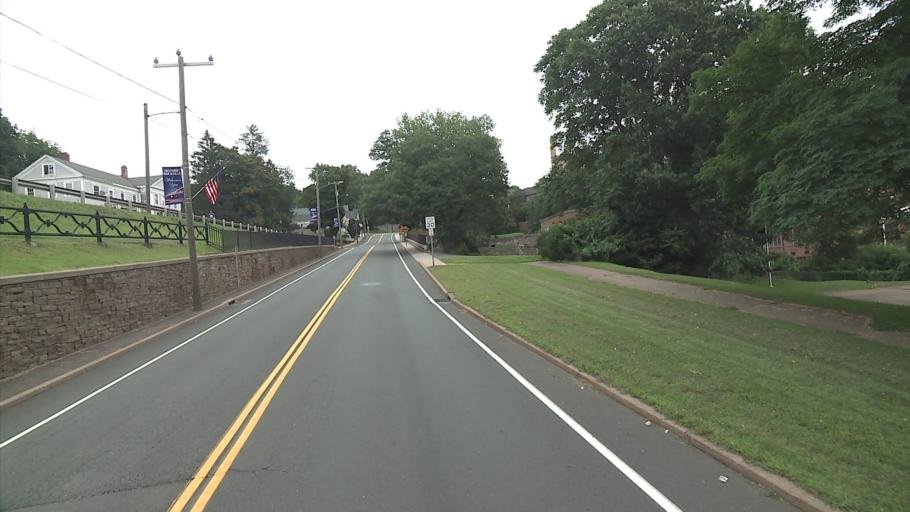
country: US
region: Connecticut
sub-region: Tolland County
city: Rockville
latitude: 41.8678
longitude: -72.4457
